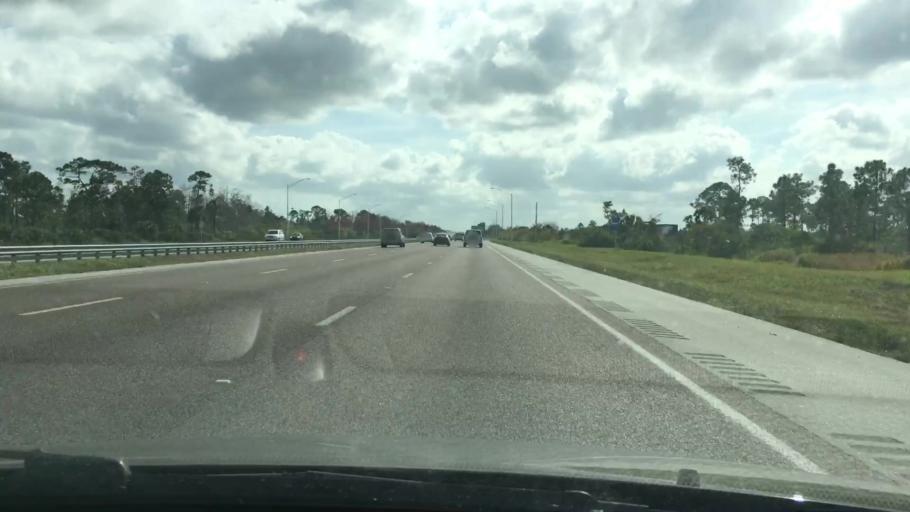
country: US
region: Florida
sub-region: Volusia County
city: Oak Hill
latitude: 28.7800
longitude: -80.8965
